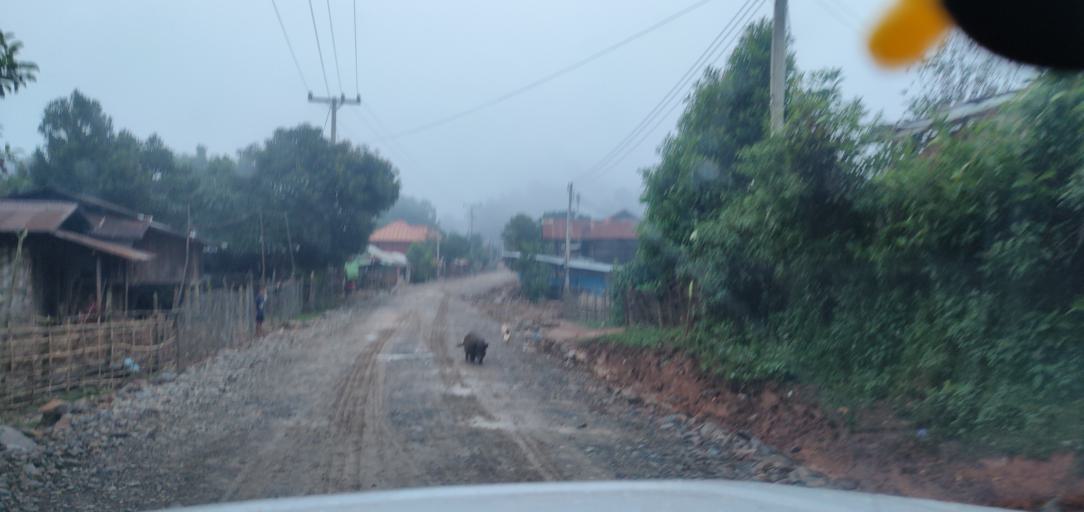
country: LA
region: Phongsali
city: Phongsali
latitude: 21.4230
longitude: 102.2535
